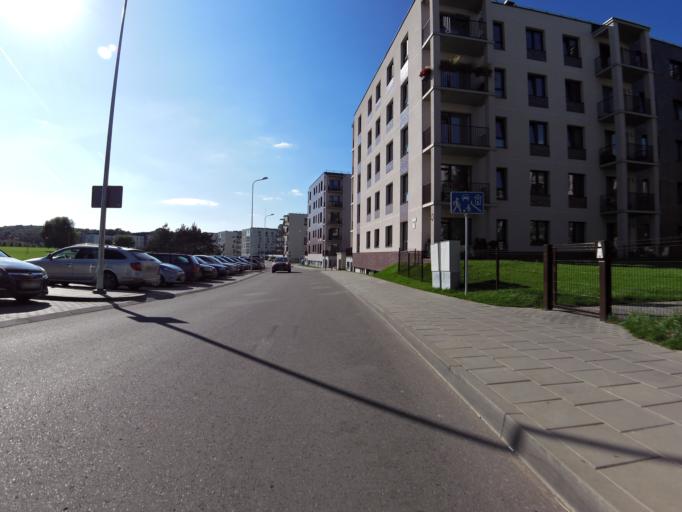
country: LT
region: Vilnius County
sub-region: Vilnius
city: Vilnius
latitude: 54.7192
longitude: 25.2816
